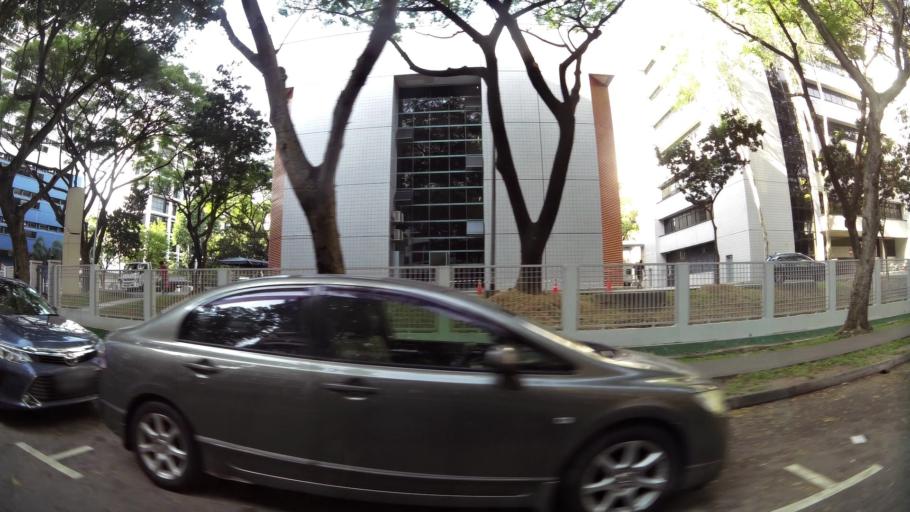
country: SG
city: Singapore
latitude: 1.3264
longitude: 103.8744
